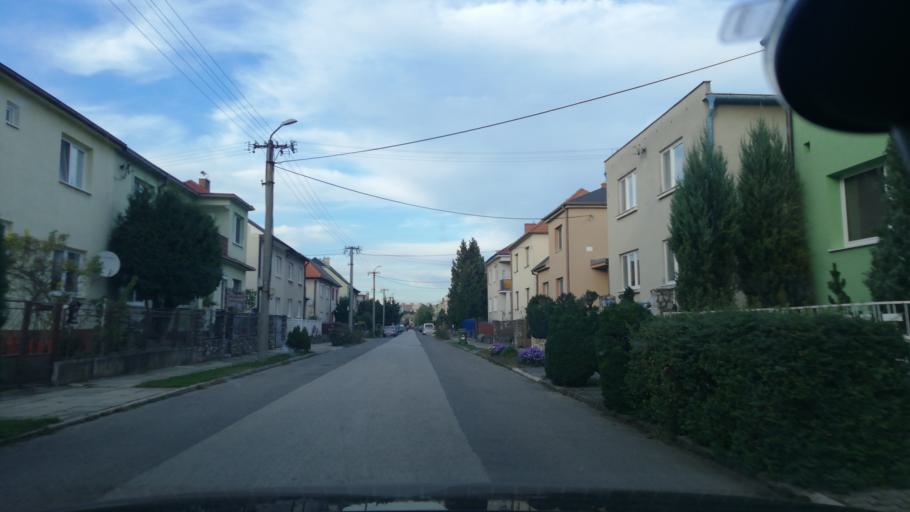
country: SK
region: Trnavsky
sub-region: Okres Skalica
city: Skalica
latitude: 48.8386
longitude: 17.2323
